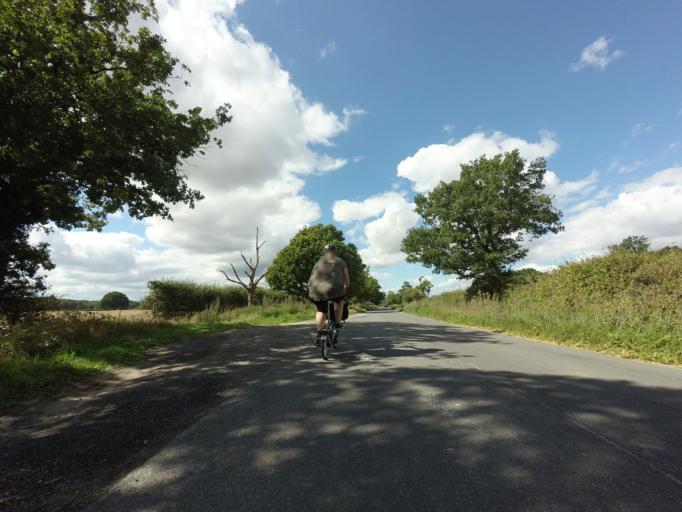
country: GB
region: England
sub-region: Kent
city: Staplehurst
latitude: 51.1526
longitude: 0.5337
